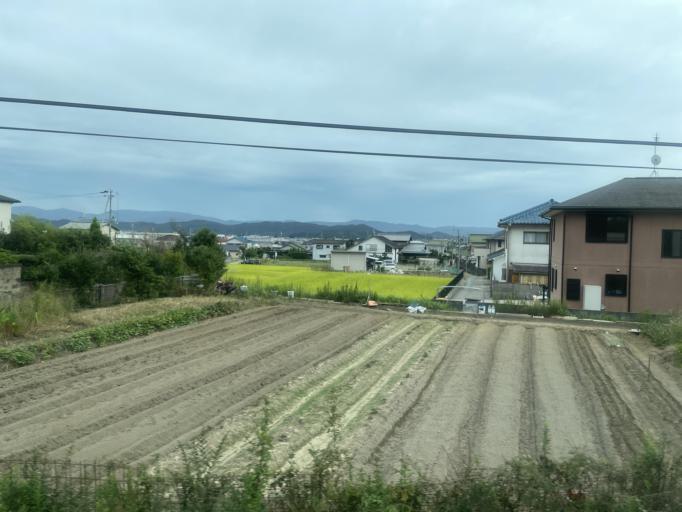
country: JP
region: Wakayama
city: Wakayama-shi
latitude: 34.2670
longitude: 135.2134
